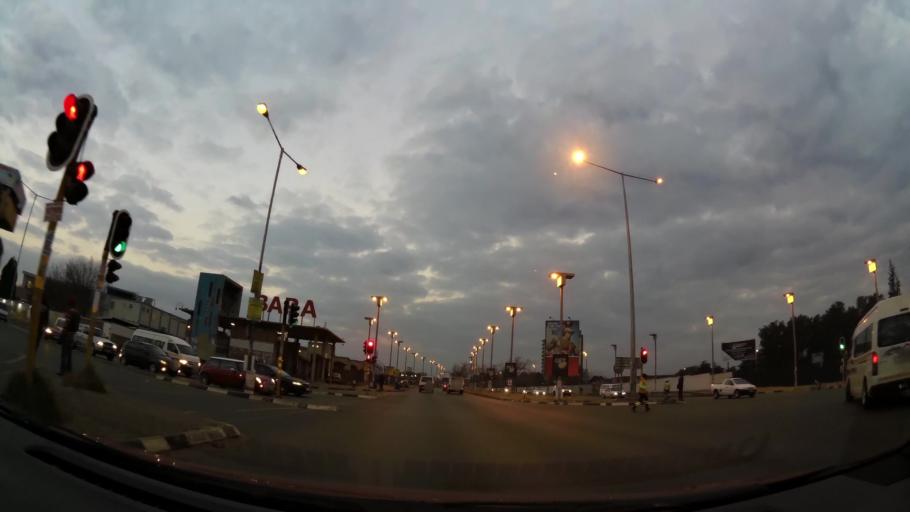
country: ZA
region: Gauteng
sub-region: City of Johannesburg Metropolitan Municipality
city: Soweto
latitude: -26.2589
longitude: 27.9346
